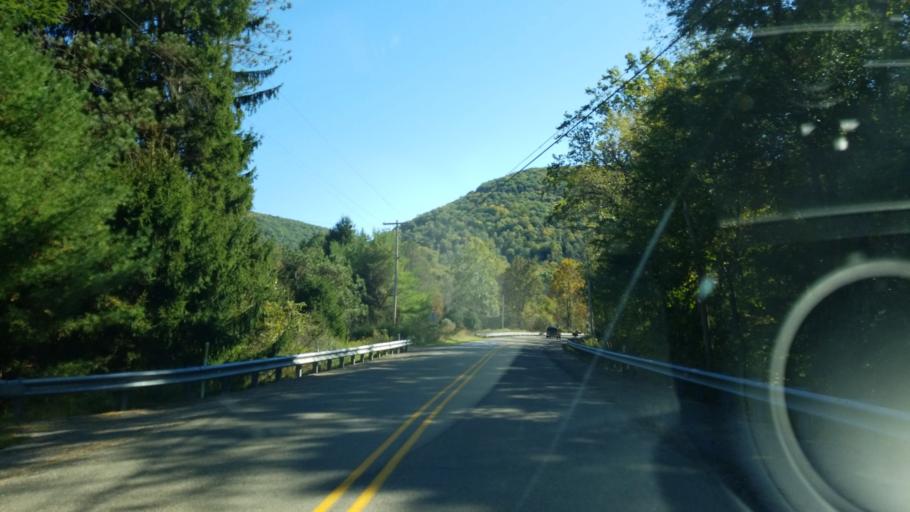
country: US
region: Pennsylvania
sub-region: Elk County
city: Saint Marys
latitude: 41.2862
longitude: -78.3943
